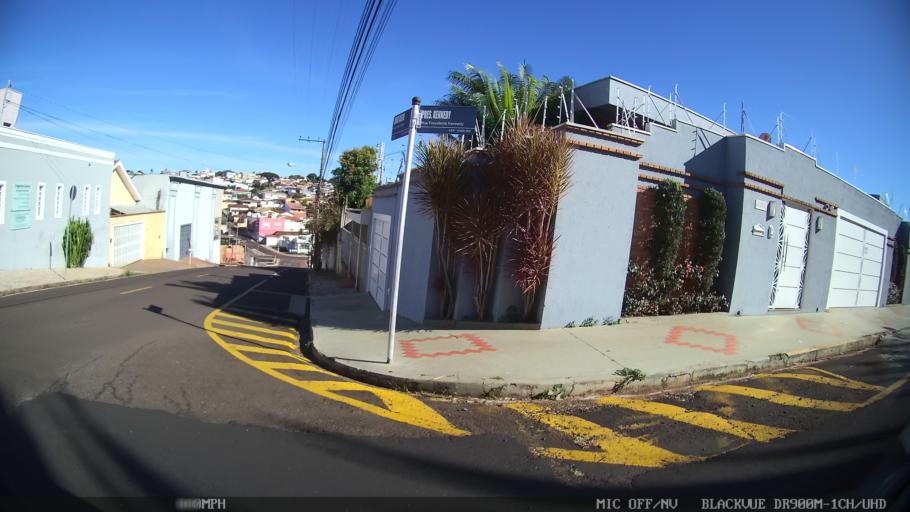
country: BR
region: Sao Paulo
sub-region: Franca
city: Franca
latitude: -20.5410
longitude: -47.4068
